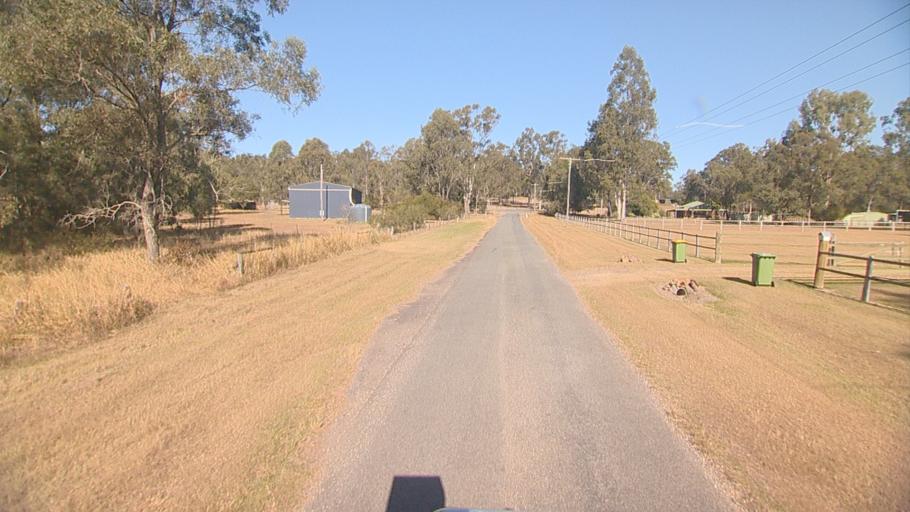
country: AU
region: Queensland
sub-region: Logan
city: Cedar Vale
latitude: -27.8649
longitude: 153.0264
